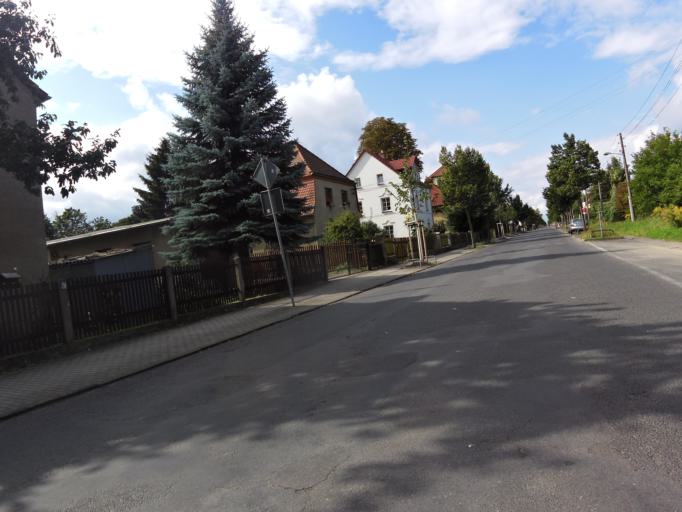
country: DE
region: Saxony
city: Rackwitz
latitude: 51.3906
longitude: 12.3706
